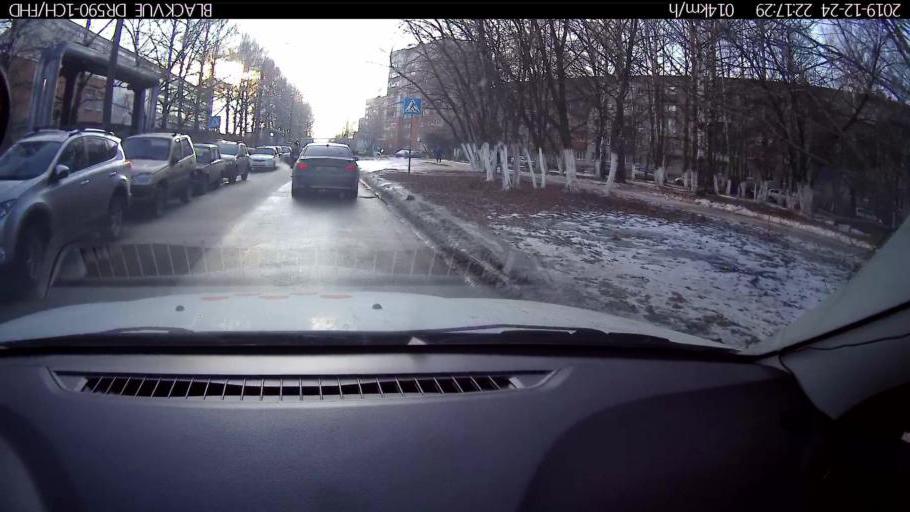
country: RU
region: Nizjnij Novgorod
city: Nizhniy Novgorod
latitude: 56.2417
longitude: 43.9725
